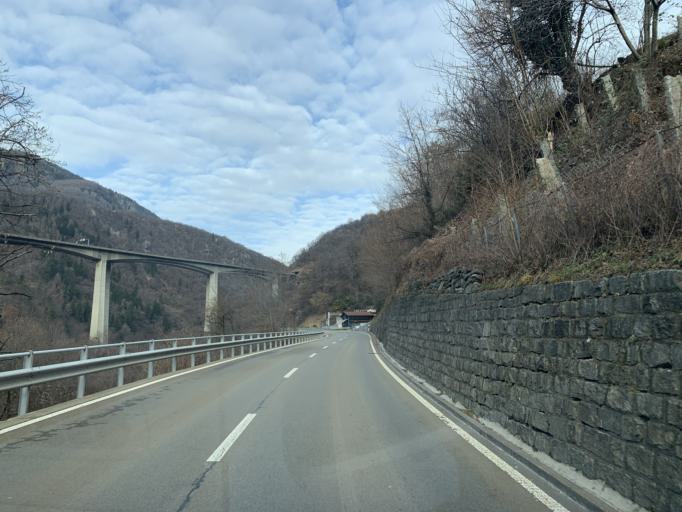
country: CH
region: Ticino
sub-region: Blenio District
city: Cancori
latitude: 46.4174
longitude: 8.8638
